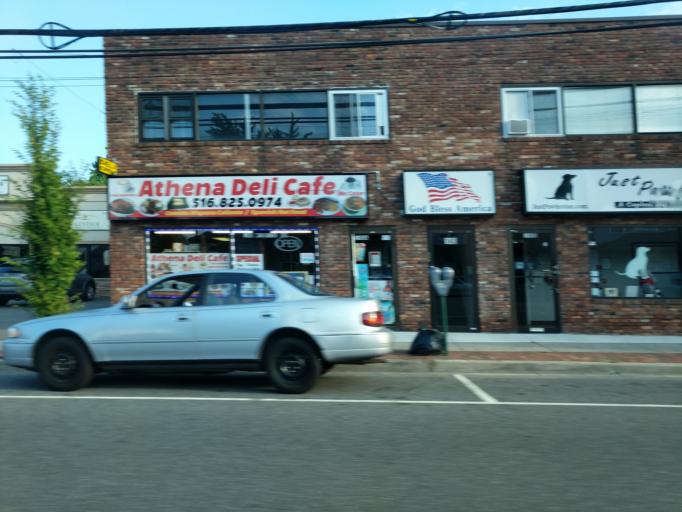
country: US
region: New York
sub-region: Nassau County
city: Lynbrook
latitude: 40.6583
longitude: -73.6630
